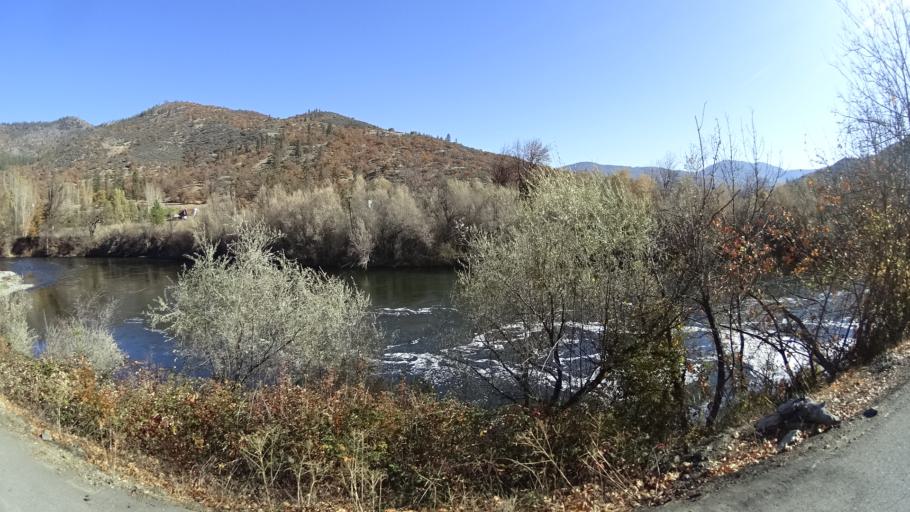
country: US
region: California
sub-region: Siskiyou County
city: Yreka
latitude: 41.8385
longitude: -122.8720
